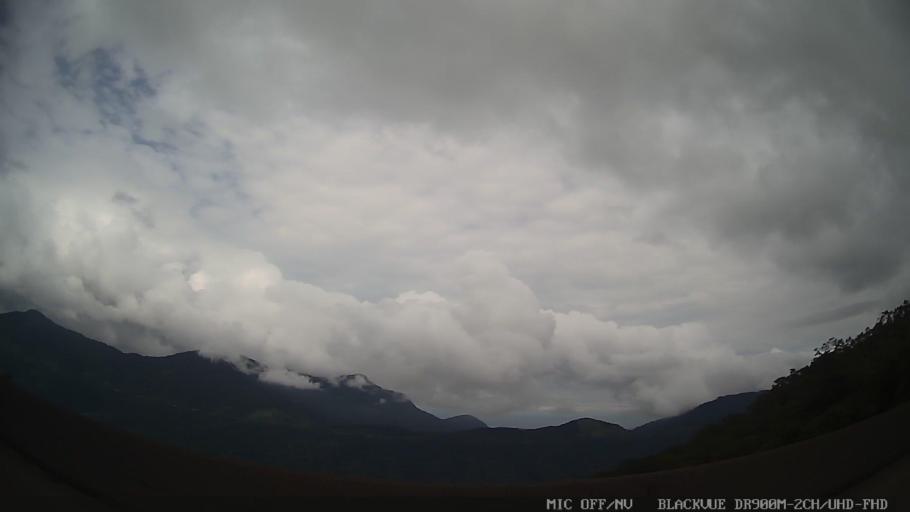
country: BR
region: Sao Paulo
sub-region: Cubatao
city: Cubatao
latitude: -23.9256
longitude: -46.5401
